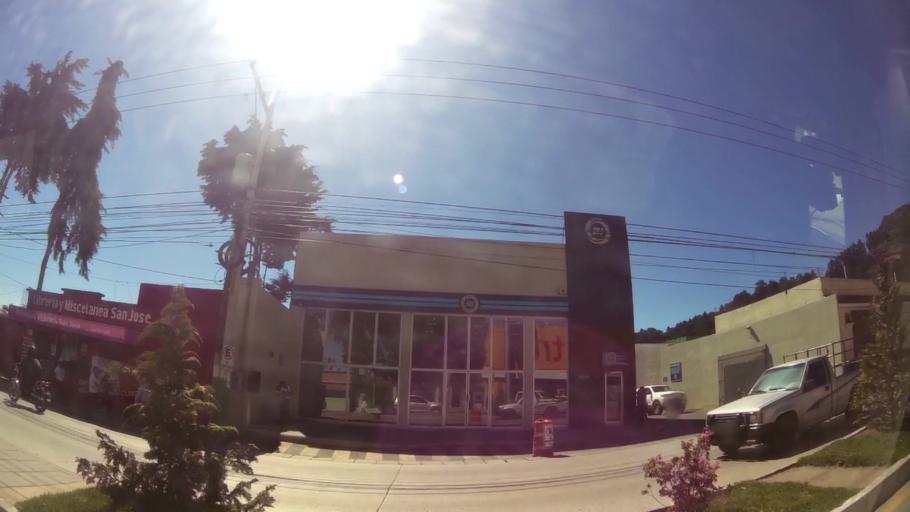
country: GT
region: Guatemala
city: San Jose Pinula
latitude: 14.5465
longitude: -90.4165
